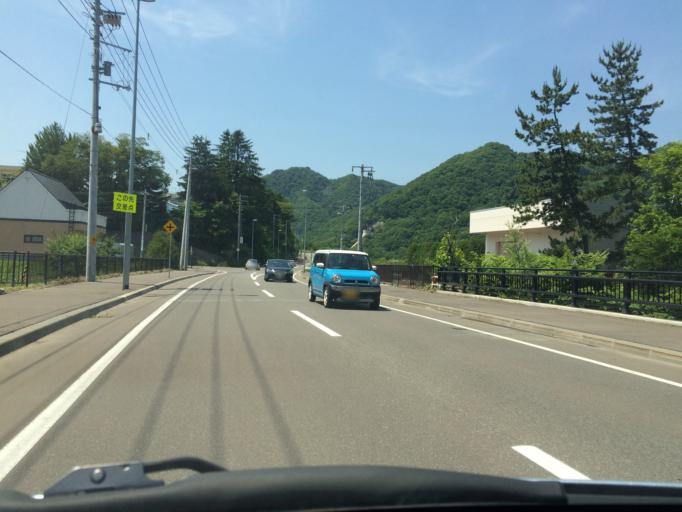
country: JP
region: Hokkaido
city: Sapporo
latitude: 42.9646
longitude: 141.2669
